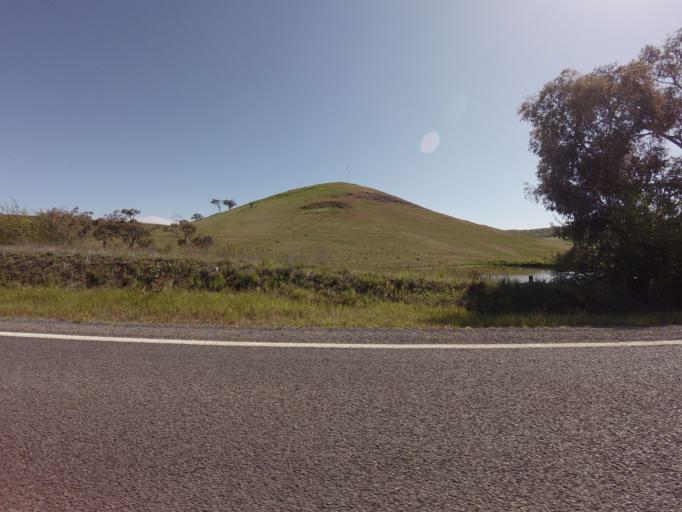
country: AU
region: Tasmania
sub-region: Derwent Valley
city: New Norfolk
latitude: -42.5734
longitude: 146.8821
